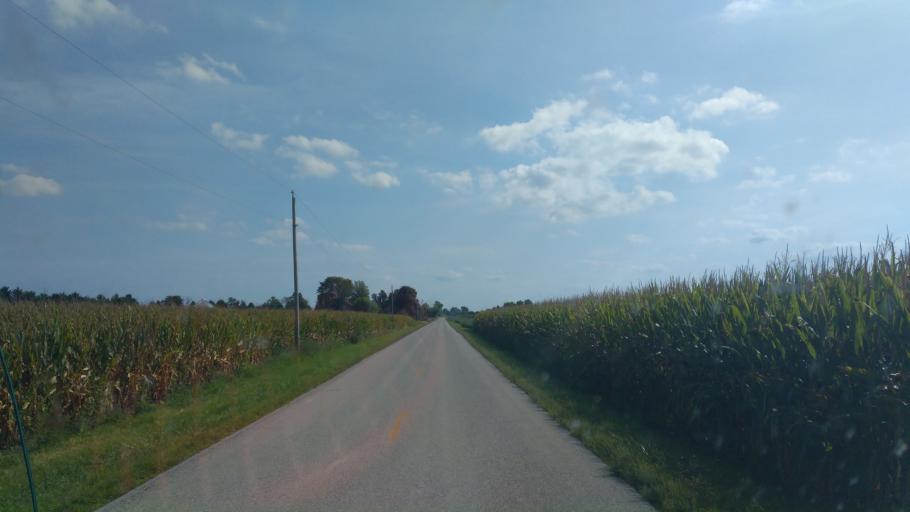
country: US
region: Ohio
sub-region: Hardin County
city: Forest
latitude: 40.6991
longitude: -83.5144
